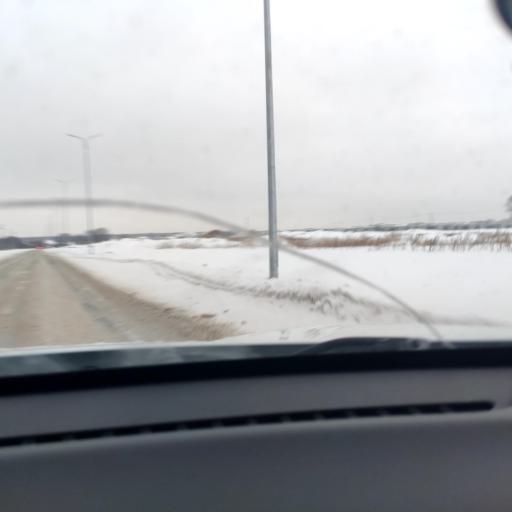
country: RU
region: Tatarstan
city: Osinovo
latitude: 55.8606
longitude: 48.8978
